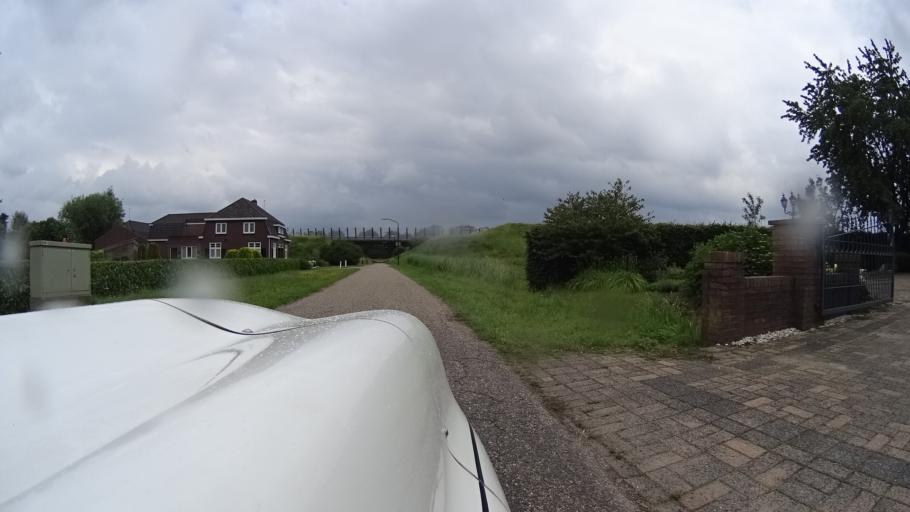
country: NL
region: North Brabant
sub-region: Gemeente Veghel
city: Eerde
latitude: 51.6059
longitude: 5.5077
